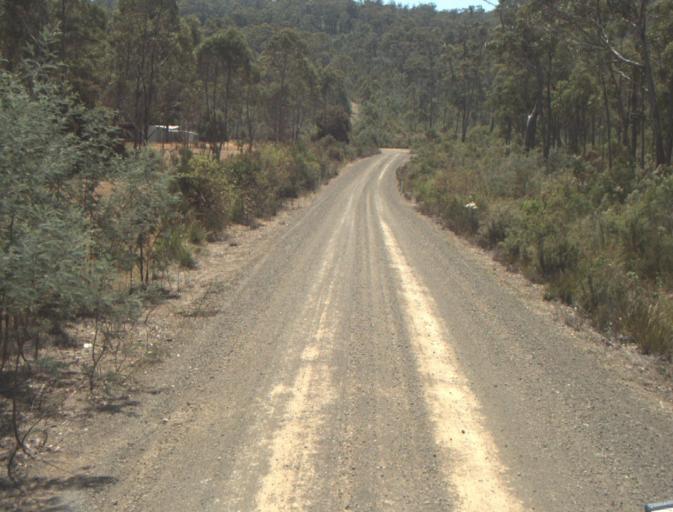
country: AU
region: Tasmania
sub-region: Launceston
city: Mayfield
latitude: -41.2738
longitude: 147.0992
